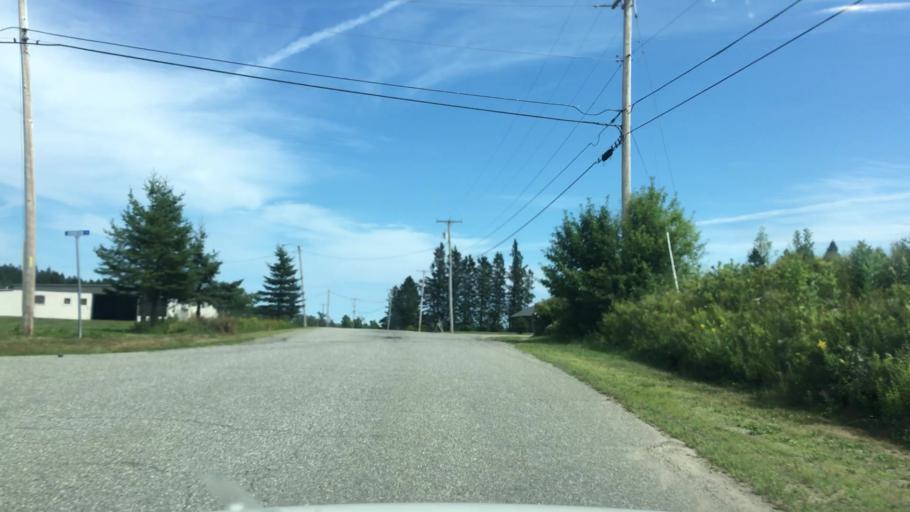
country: US
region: Maine
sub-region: Washington County
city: Eastport
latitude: 44.9271
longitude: -67.0292
